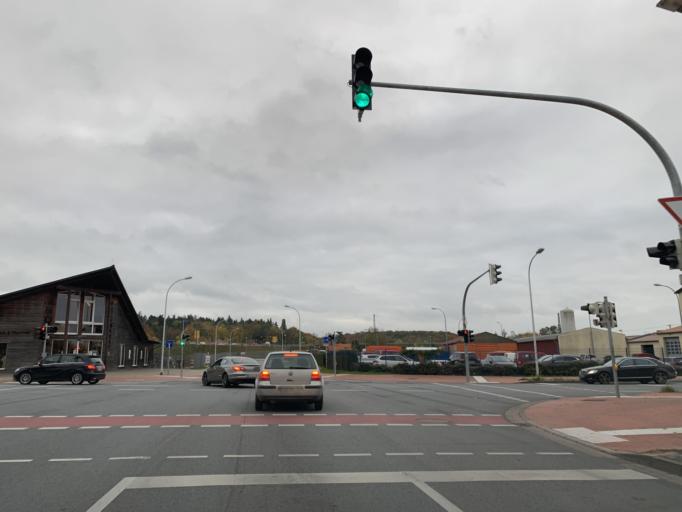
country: DE
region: Mecklenburg-Vorpommern
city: Neubrandenburg
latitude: 53.5608
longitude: 13.2829
